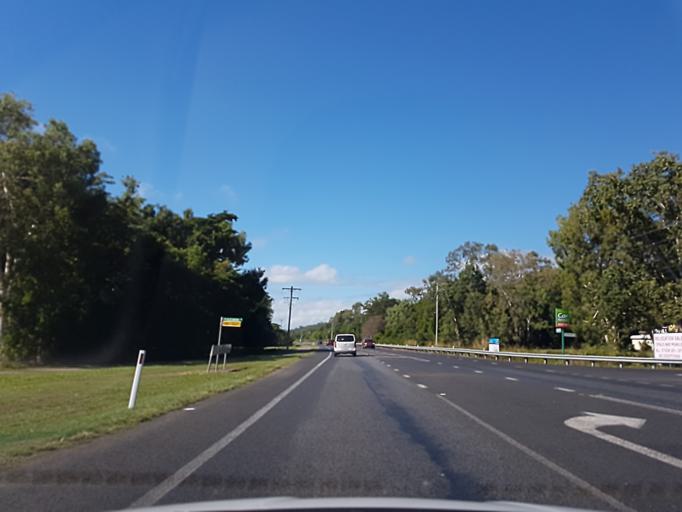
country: AU
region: Queensland
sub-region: Cairns
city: Palm Cove
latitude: -16.7587
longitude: 145.6637
